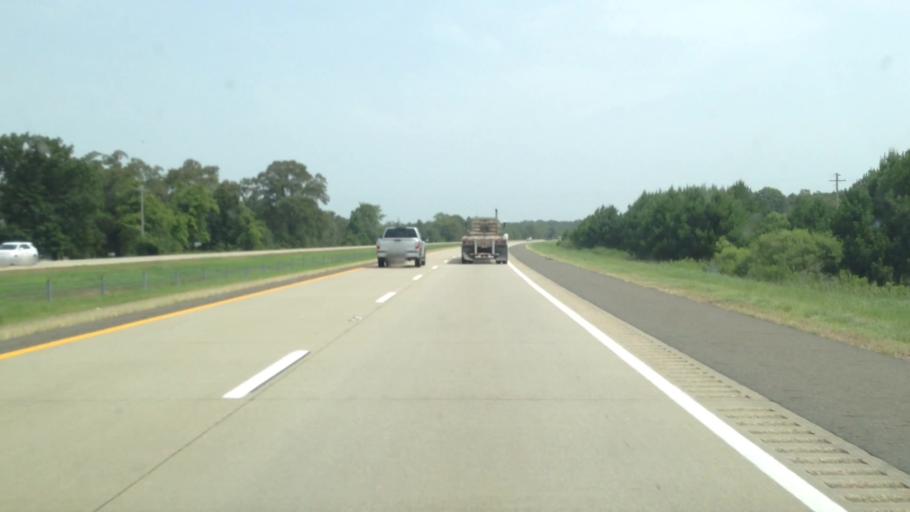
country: US
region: Texas
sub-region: Cass County
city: Queen City
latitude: 33.1974
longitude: -93.8774
